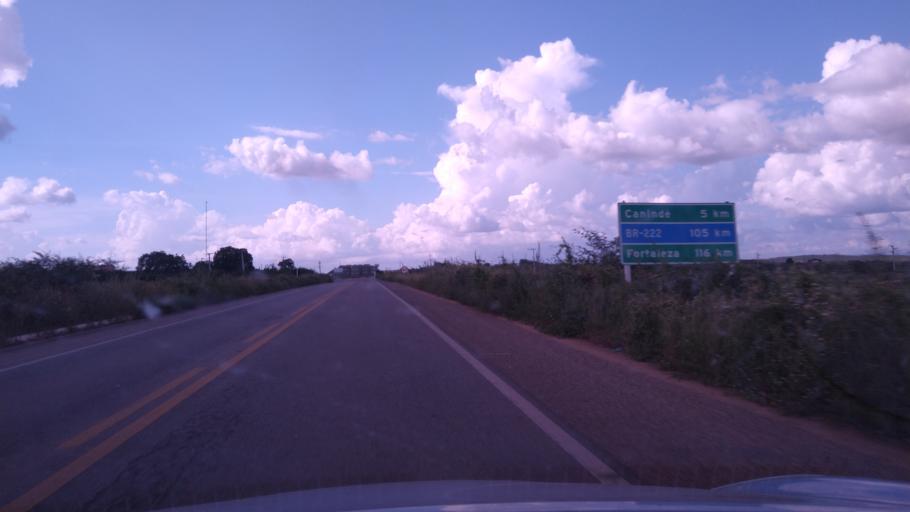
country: BR
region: Ceara
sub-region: Caninde
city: Caninde
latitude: -4.3887
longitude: -39.3130
